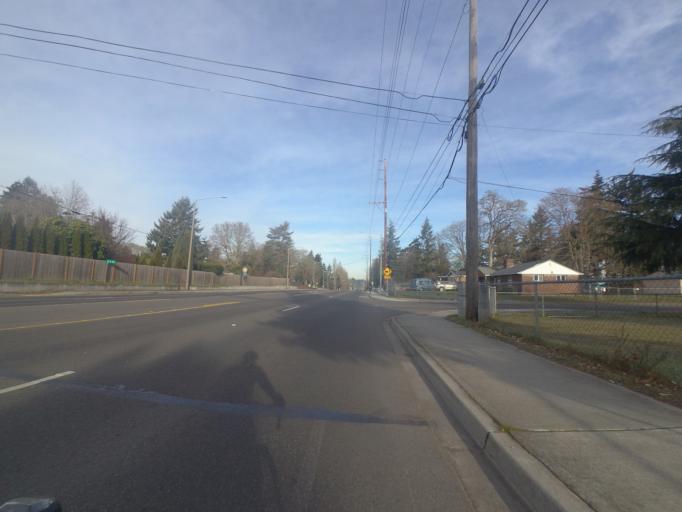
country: US
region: Washington
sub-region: Pierce County
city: Lakewood
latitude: 47.1817
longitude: -122.5181
